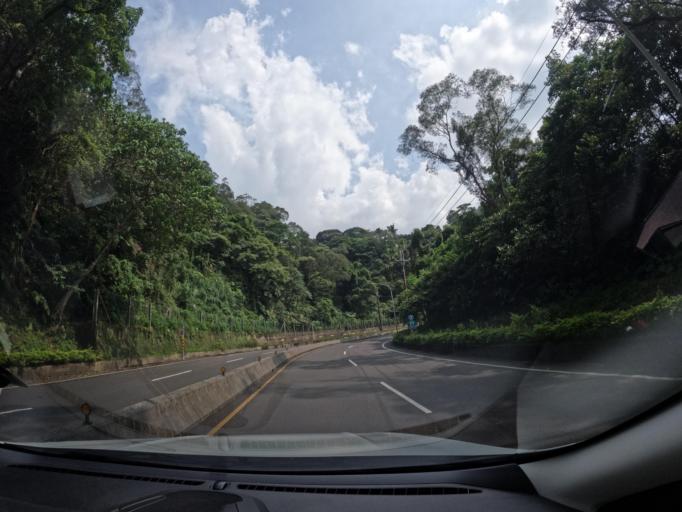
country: TW
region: Taiwan
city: Daxi
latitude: 24.8929
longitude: 121.3350
